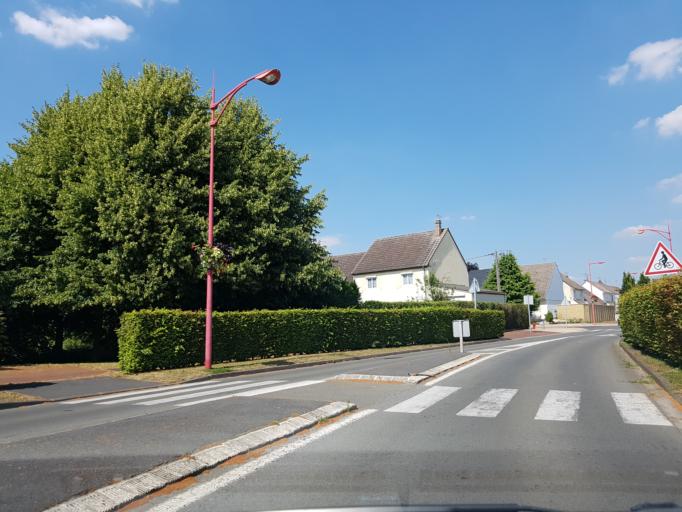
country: FR
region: Nord-Pas-de-Calais
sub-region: Departement du Nord
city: Roeulx
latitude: 50.3073
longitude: 3.3260
